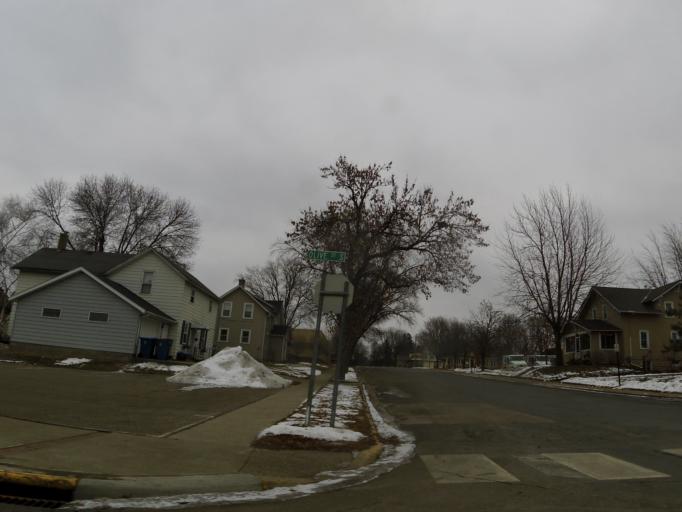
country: US
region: Minnesota
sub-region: Carver County
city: Waconia
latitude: 44.8483
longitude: -93.7876
